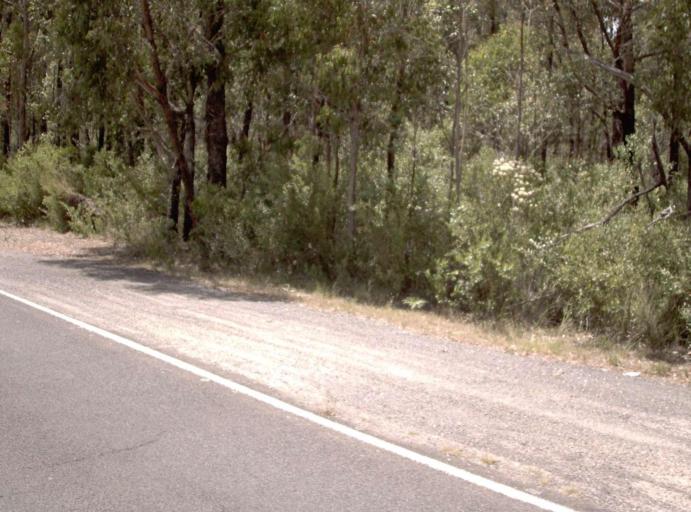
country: AU
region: Victoria
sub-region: Latrobe
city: Moe
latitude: -38.0875
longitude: 146.3196
